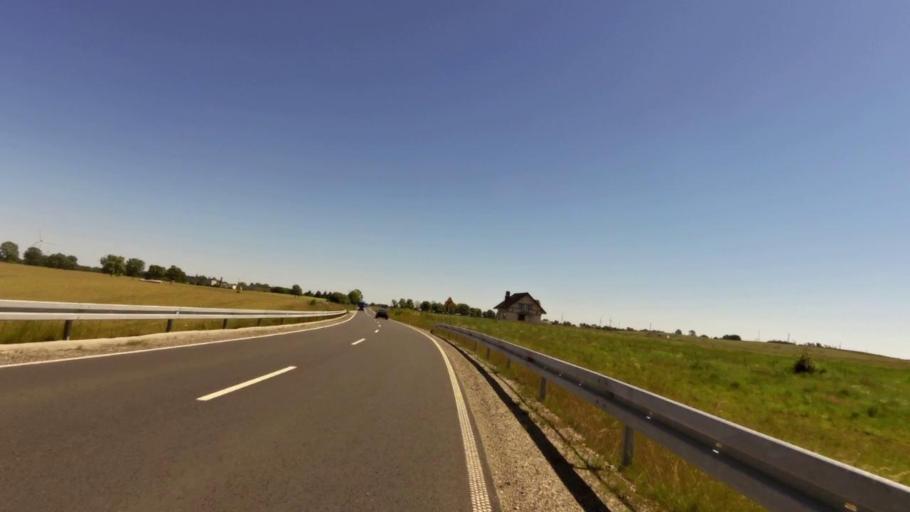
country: PL
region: West Pomeranian Voivodeship
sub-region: Powiat kolobrzeski
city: Goscino
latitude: 54.0441
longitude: 15.6527
